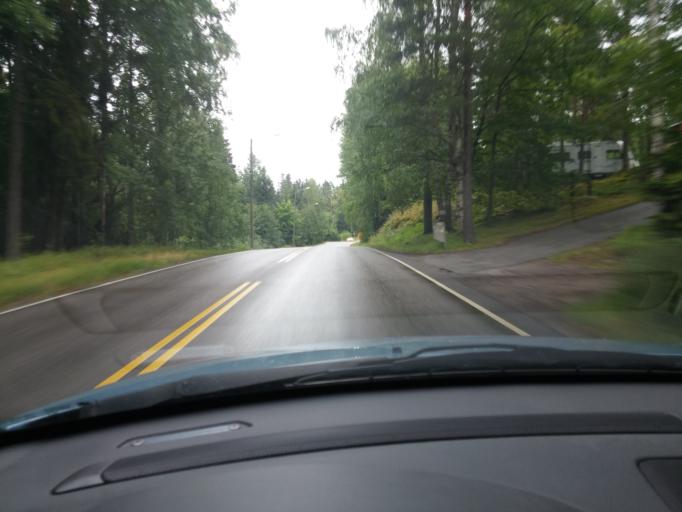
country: FI
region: Uusimaa
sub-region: Helsinki
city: Kauniainen
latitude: 60.3472
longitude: 24.7348
